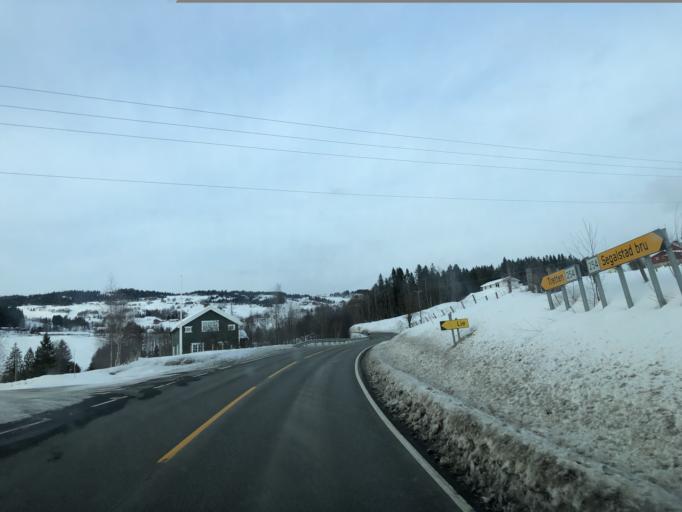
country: NO
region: Oppland
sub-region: Gausdal
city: Segalstad bru
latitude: 61.2730
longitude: 10.1450
